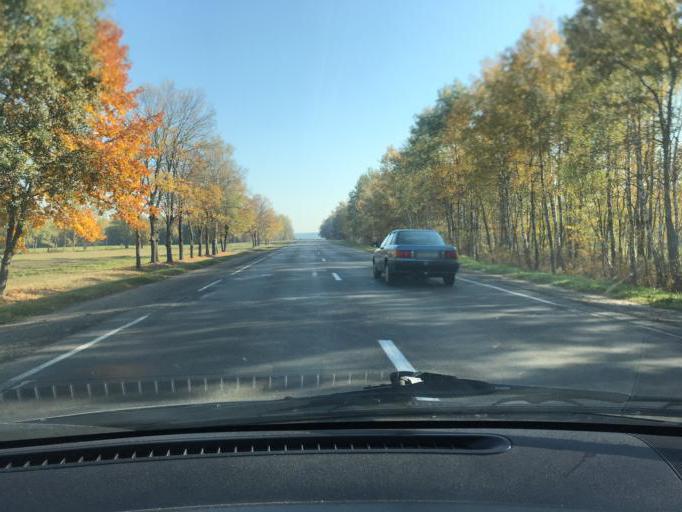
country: BY
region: Brest
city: Luninyets
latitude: 52.2747
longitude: 26.8902
